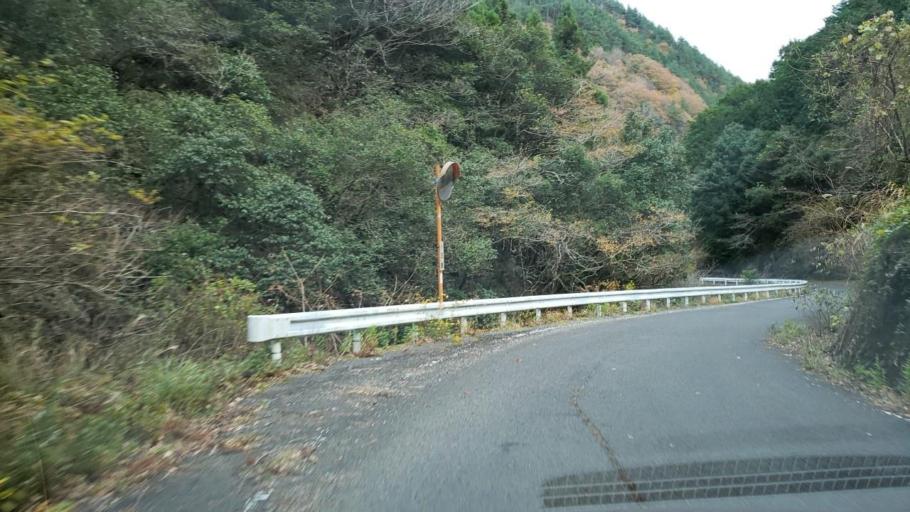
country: JP
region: Tokushima
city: Wakimachi
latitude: 34.1417
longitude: 134.2305
